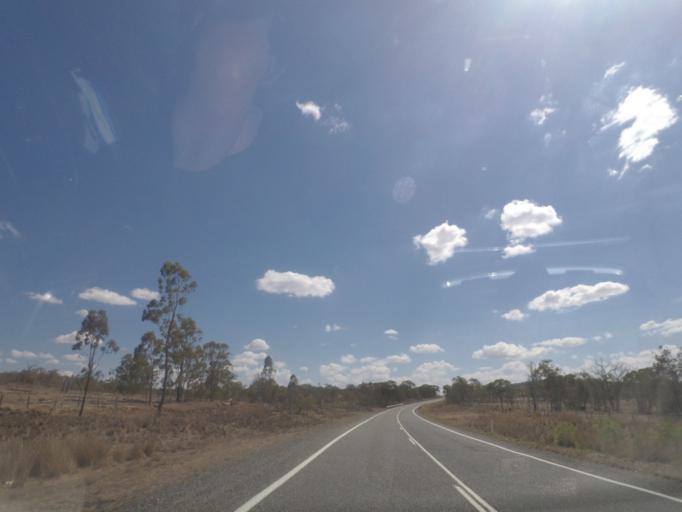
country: AU
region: Queensland
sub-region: Southern Downs
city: Warwick
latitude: -28.2168
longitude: 151.5613
